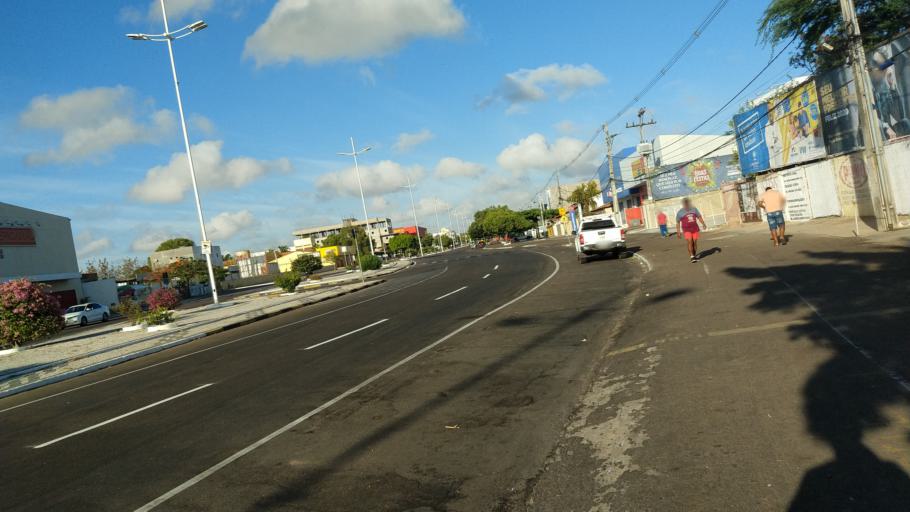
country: BR
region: Bahia
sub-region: Paulo Afonso
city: Paulo Afonso
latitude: -9.3982
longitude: -38.2203
